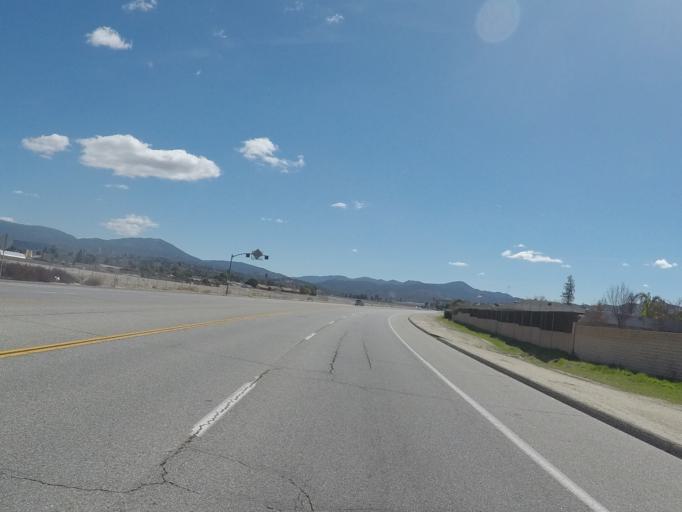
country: US
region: California
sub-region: Riverside County
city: Valle Vista
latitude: 33.7598
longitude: -116.9102
